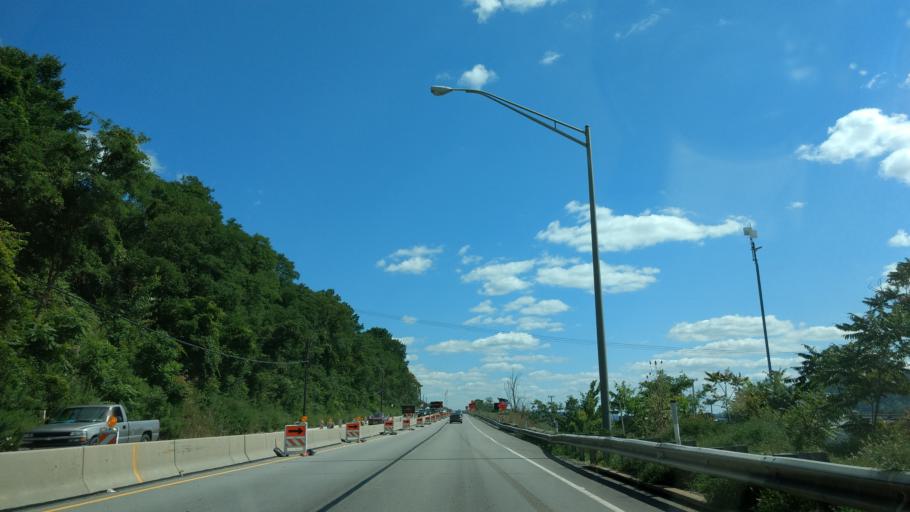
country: US
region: Pennsylvania
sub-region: Beaver County
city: Freedom
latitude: 40.6764
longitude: -80.2478
